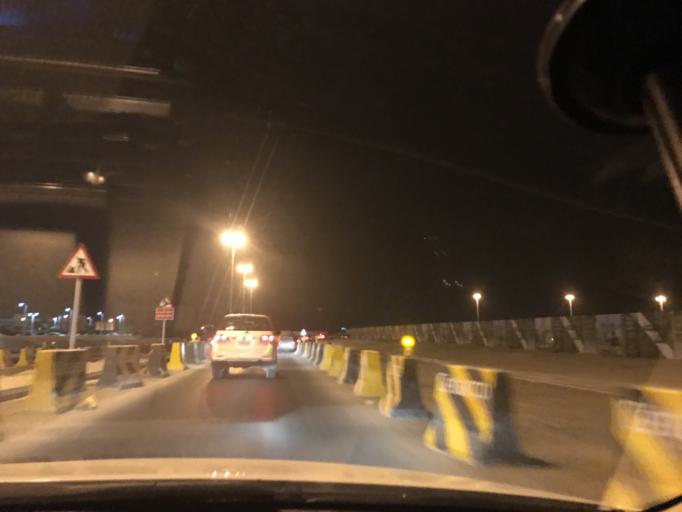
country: BH
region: Muharraq
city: Al Muharraq
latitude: 26.3045
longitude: 50.6274
